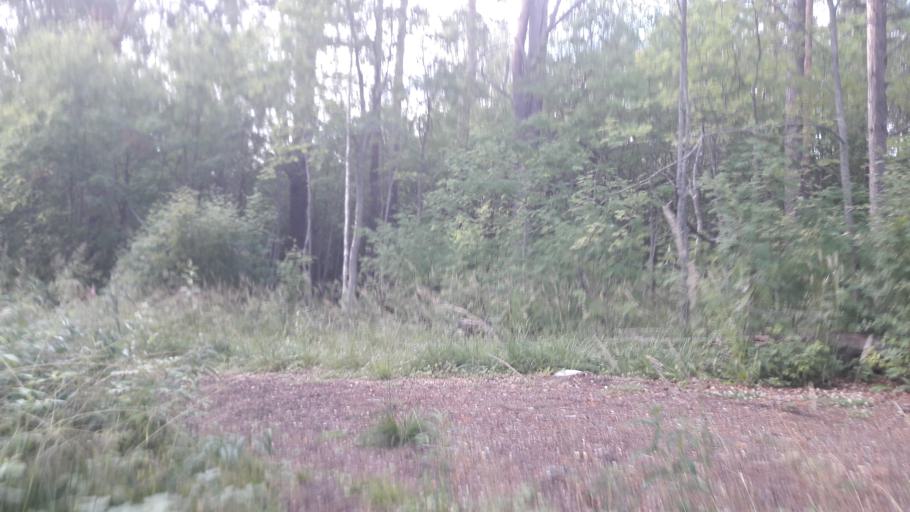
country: FI
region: North Karelia
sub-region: Joensuu
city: Joensuu
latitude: 62.5737
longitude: 29.8141
